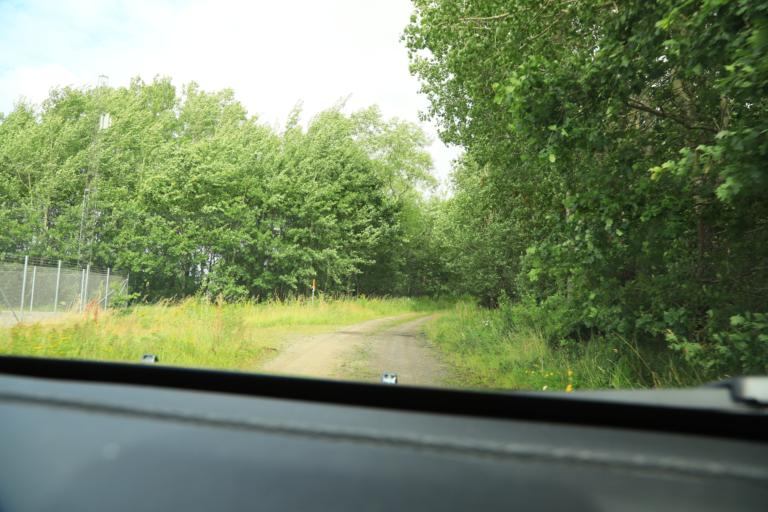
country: SE
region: Halland
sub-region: Varbergs Kommun
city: Traslovslage
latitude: 57.1219
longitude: 12.3153
